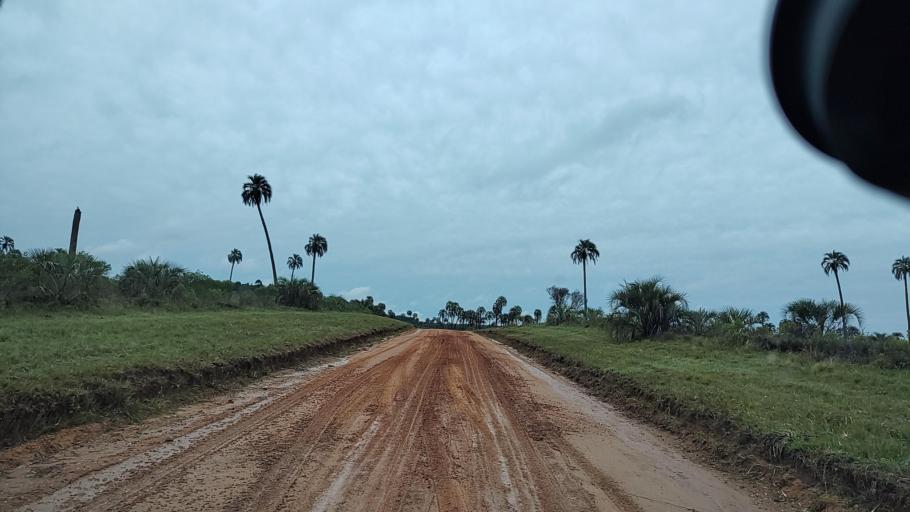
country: AR
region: Entre Rios
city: Ubajay
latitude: -31.8513
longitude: -58.3127
